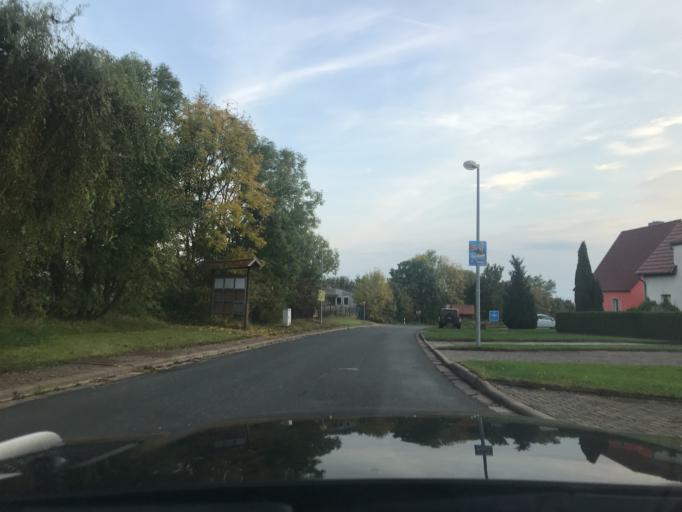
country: DE
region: Thuringia
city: Sollstedt
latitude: 51.2711
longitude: 10.4828
